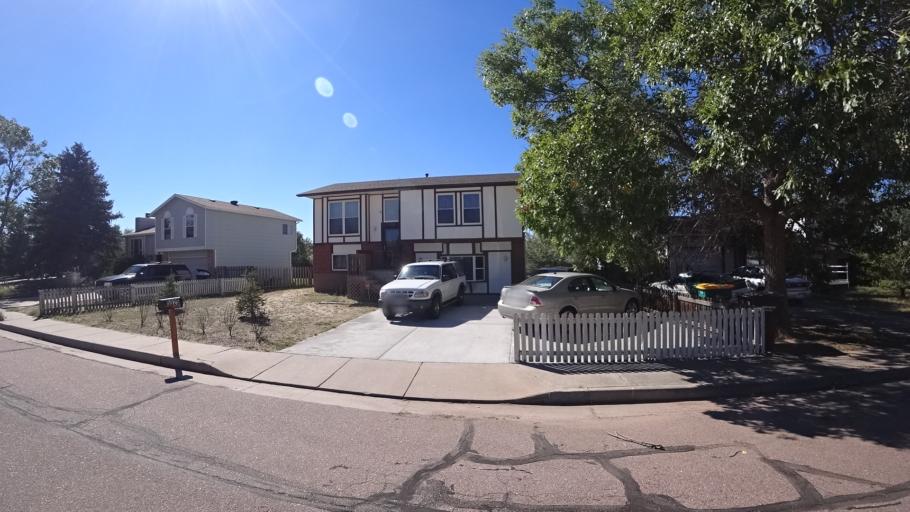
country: US
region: Colorado
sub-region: El Paso County
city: Cimarron Hills
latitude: 38.8197
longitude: -104.7341
